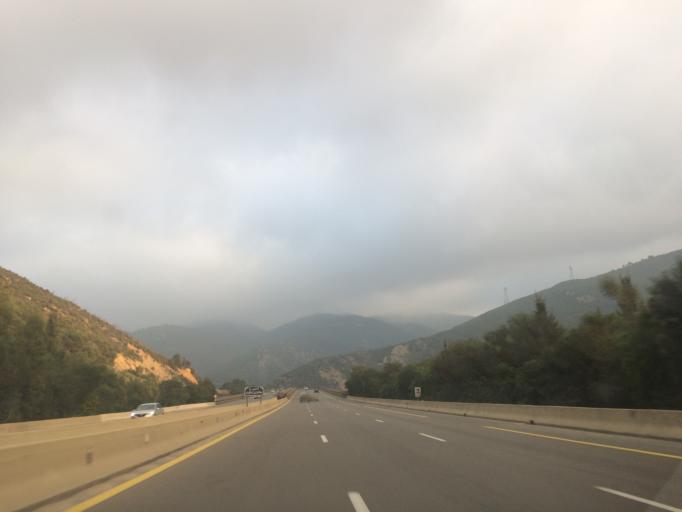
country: DZ
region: Tipaza
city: El Affroun
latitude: 36.4028
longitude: 2.5460
